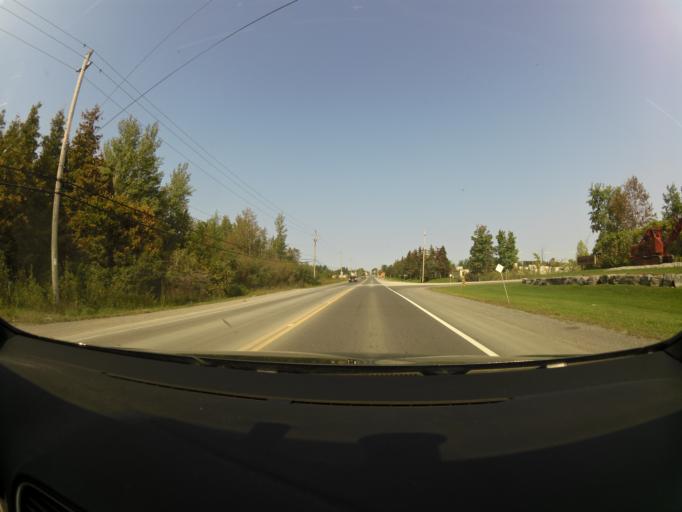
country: CA
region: Ontario
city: Bells Corners
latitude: 45.2905
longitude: -75.9688
